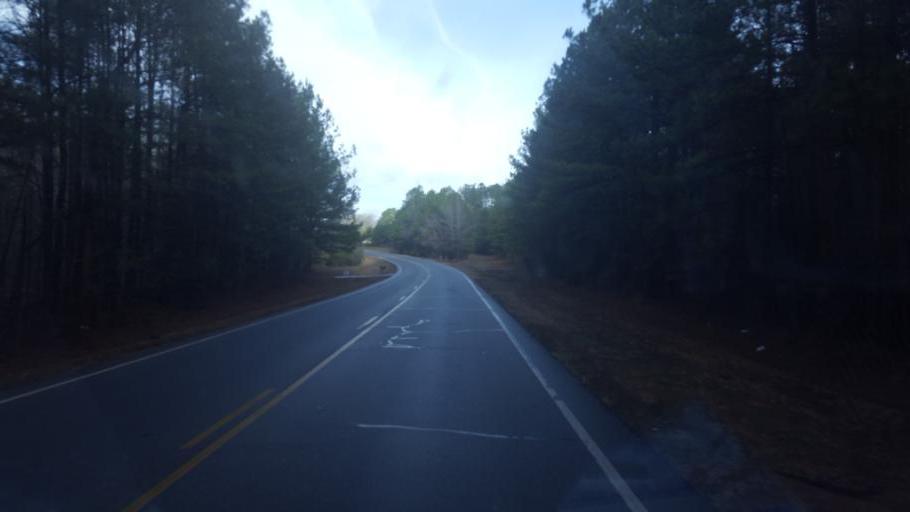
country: US
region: Georgia
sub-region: Butts County
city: Indian Springs
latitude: 33.2448
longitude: -83.8845
